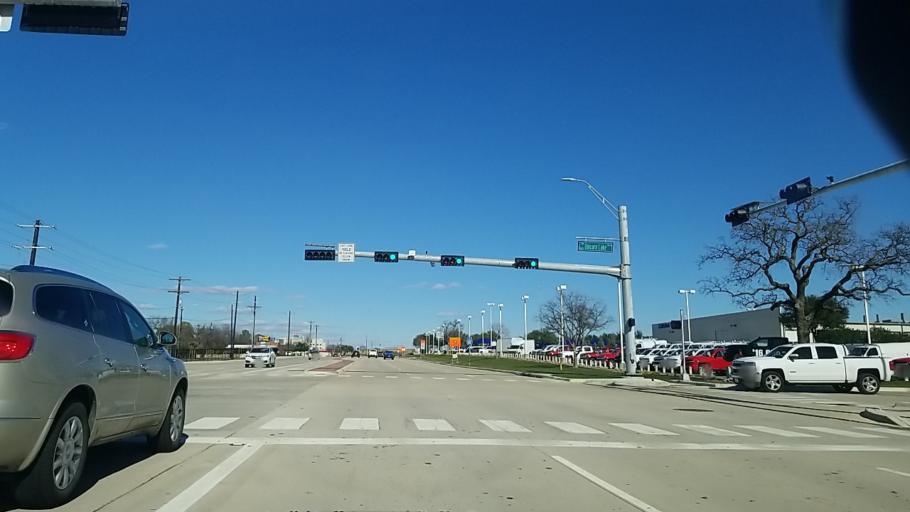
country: US
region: Texas
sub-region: Denton County
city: Corinth
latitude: 33.1693
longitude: -97.0908
